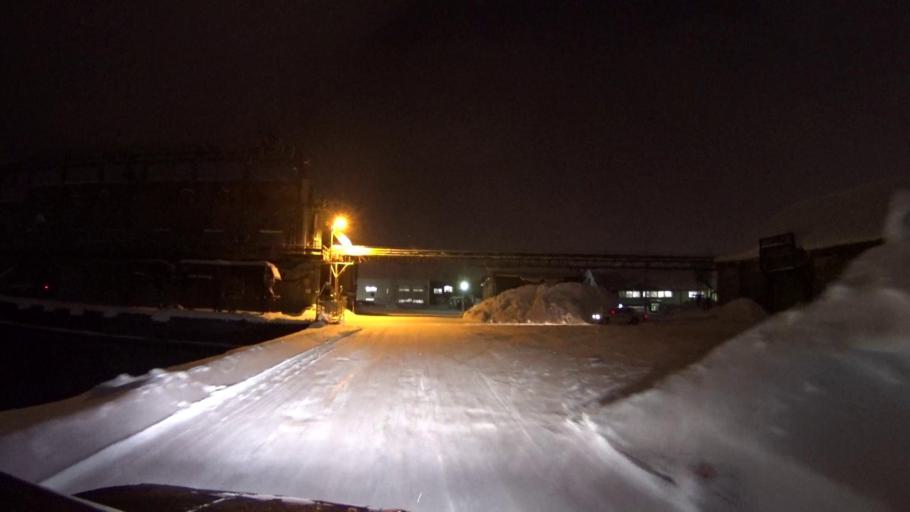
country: JP
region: Hokkaido
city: Otaru
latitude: 43.1982
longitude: 141.0059
